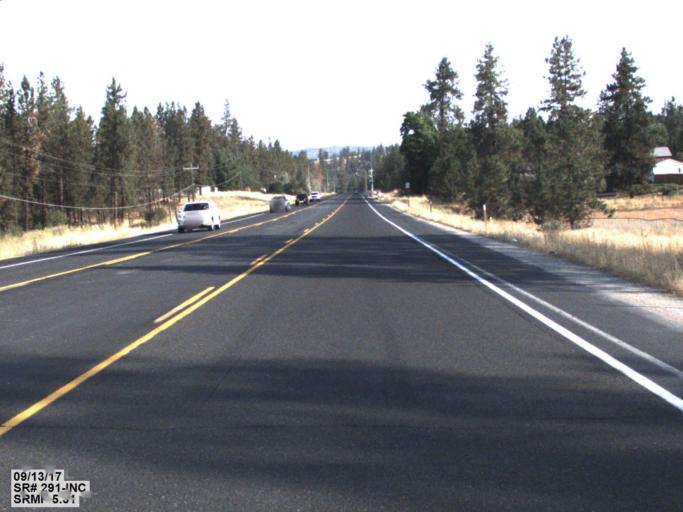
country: US
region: Washington
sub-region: Spokane County
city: Town and Country
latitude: 47.7384
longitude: -117.5075
